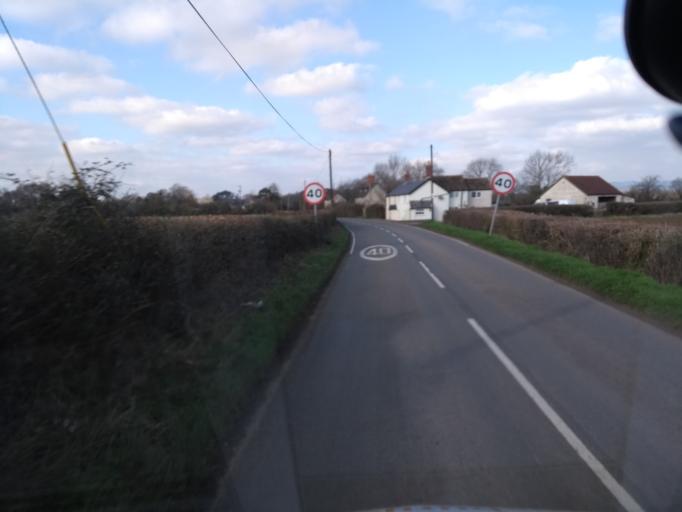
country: GB
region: England
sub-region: Somerset
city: Taunton
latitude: 50.9866
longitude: -3.0671
